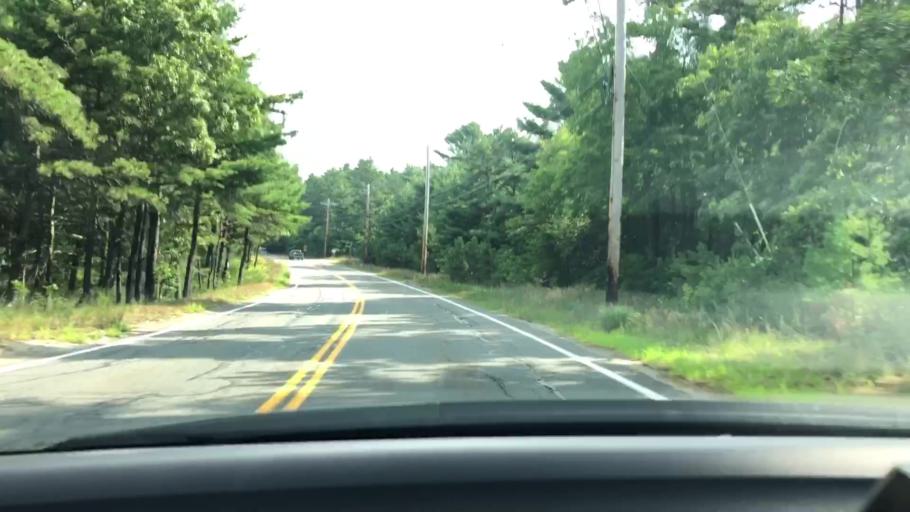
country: US
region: Massachusetts
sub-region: Plymouth County
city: White Island Shores
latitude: 41.8861
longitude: -70.5872
